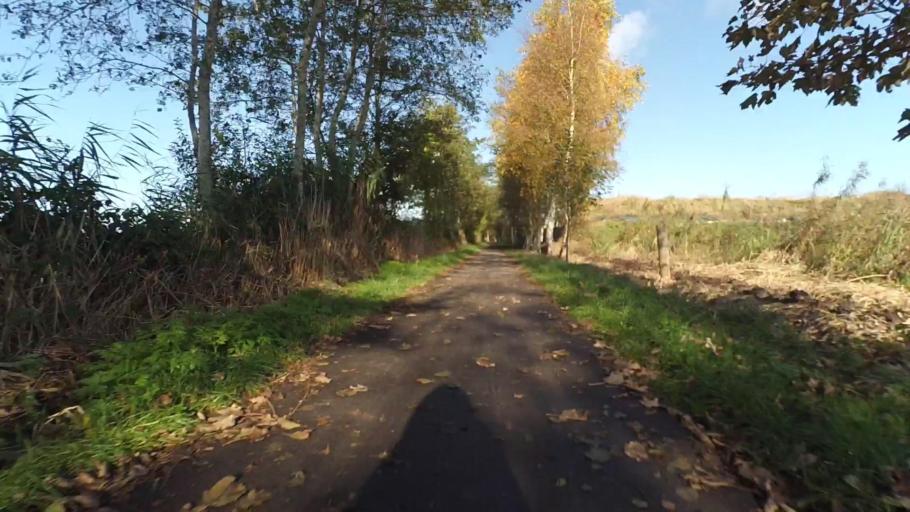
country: NL
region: Gelderland
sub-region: Gemeente Barneveld
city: Zwartebroek
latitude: 52.2144
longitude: 5.5351
